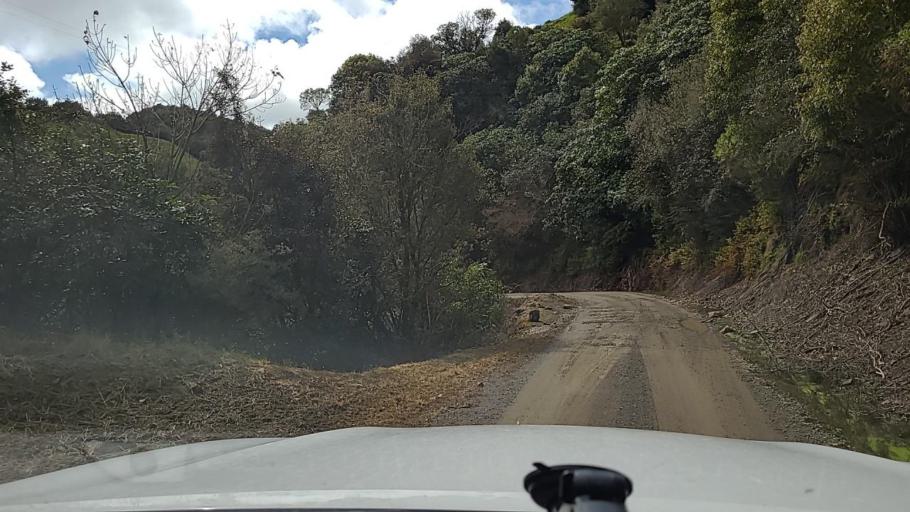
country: NZ
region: Bay of Plenty
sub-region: Opotiki District
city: Opotiki
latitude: -38.2510
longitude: 177.6066
